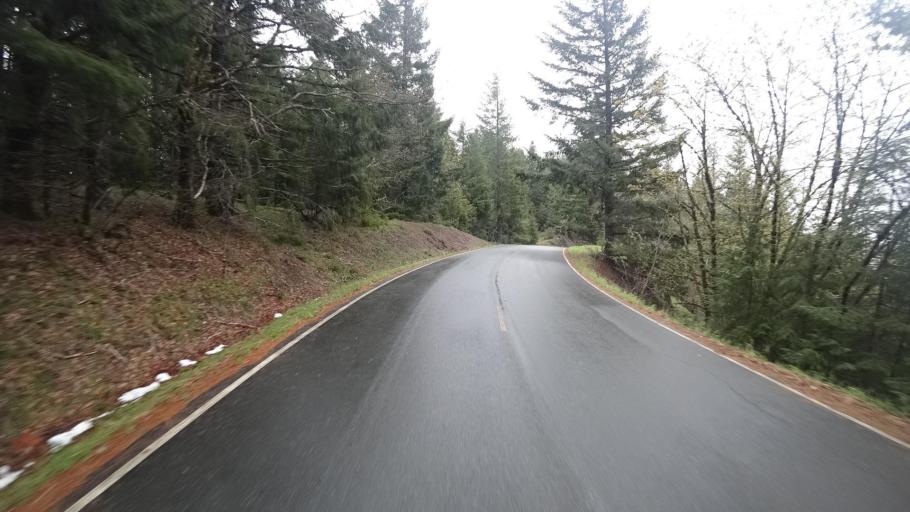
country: US
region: California
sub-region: Humboldt County
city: Westhaven-Moonstone
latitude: 41.1442
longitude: -123.8509
